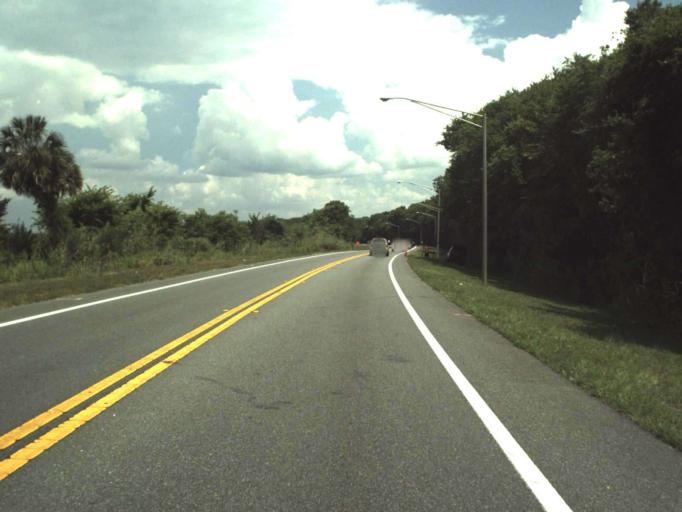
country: US
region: Florida
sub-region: Seminole County
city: Sanford
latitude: 28.8284
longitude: -81.3101
